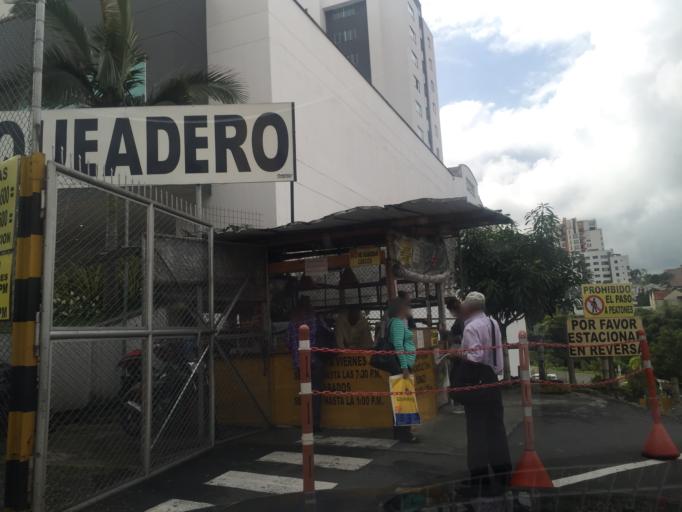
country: CO
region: Risaralda
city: Pereira
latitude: 4.8047
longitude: -75.6905
